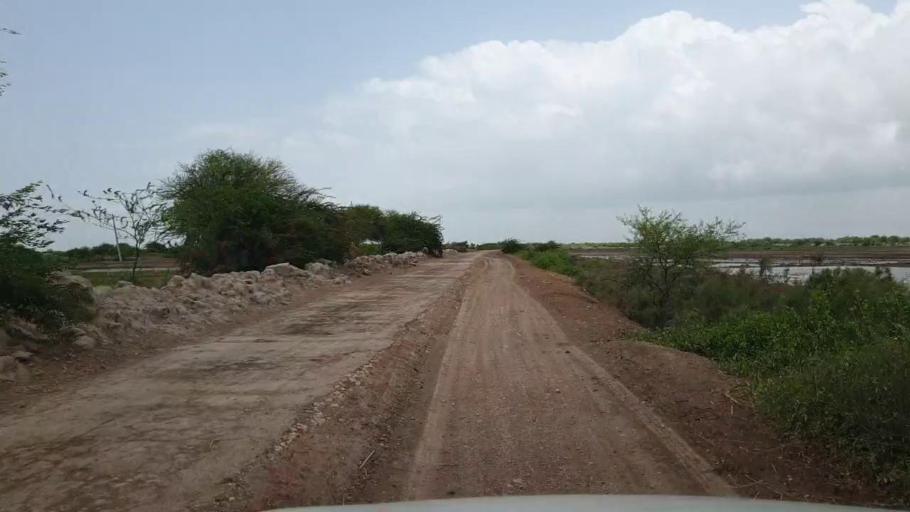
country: PK
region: Sindh
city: Kario
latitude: 24.6920
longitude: 68.6578
